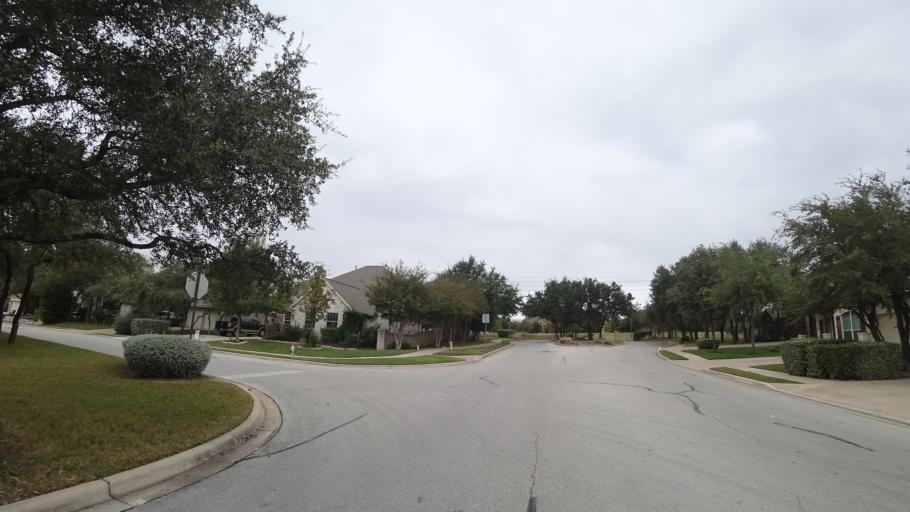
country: US
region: Texas
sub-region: Travis County
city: Bee Cave
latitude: 30.3566
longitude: -97.9062
